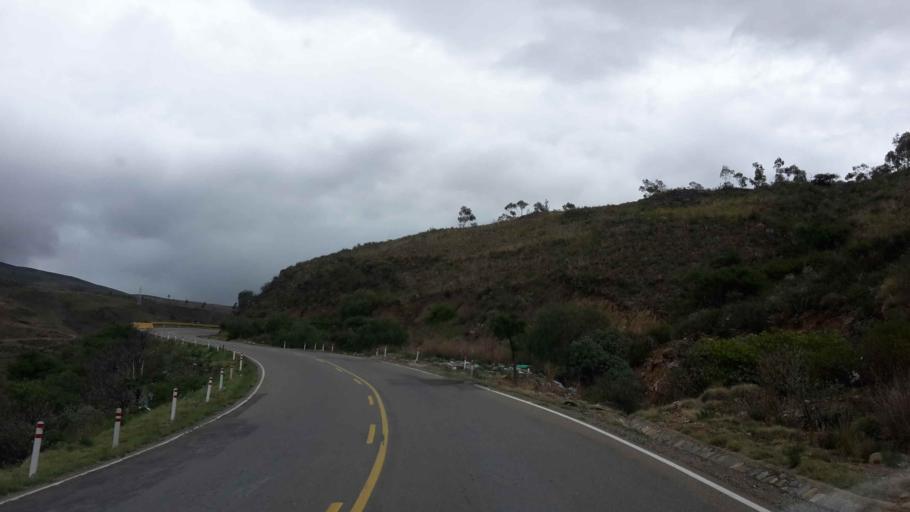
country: BO
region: Cochabamba
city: Punata
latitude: -17.4942
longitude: -65.7933
